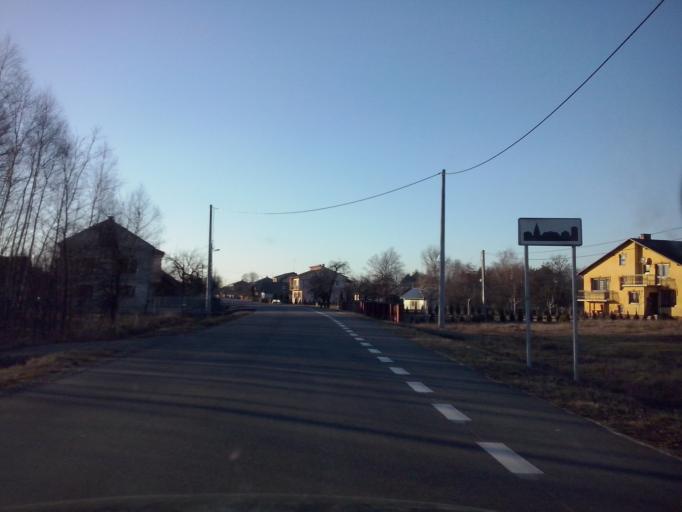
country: PL
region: Subcarpathian Voivodeship
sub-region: Powiat nizanski
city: Harasiuki
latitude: 50.4695
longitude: 22.5088
